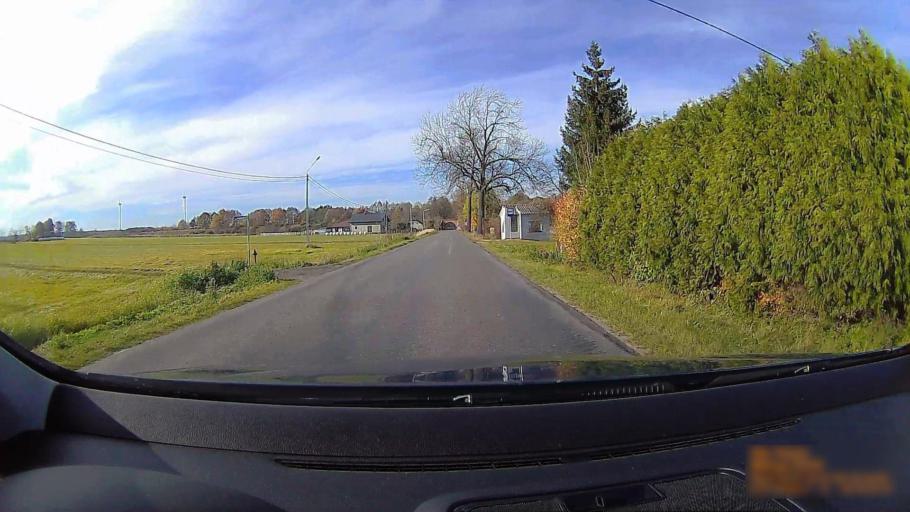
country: PL
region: Greater Poland Voivodeship
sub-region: Powiat ostrzeszowski
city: Doruchow
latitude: 51.4303
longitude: 18.0327
